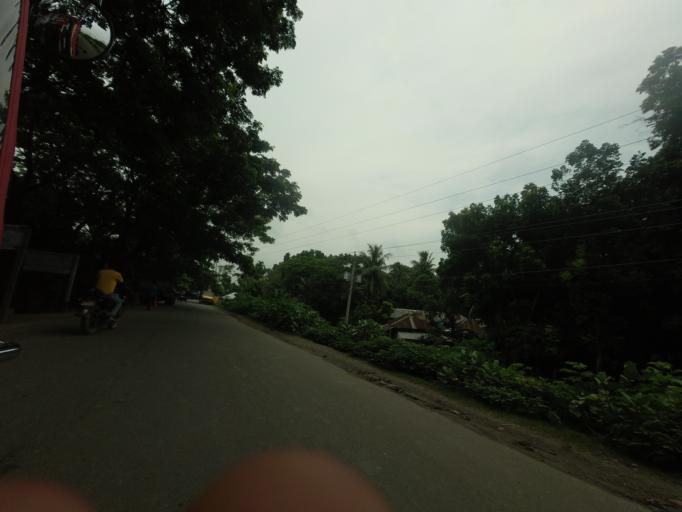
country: BD
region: Khulna
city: Kalia
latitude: 23.1835
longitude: 89.6538
